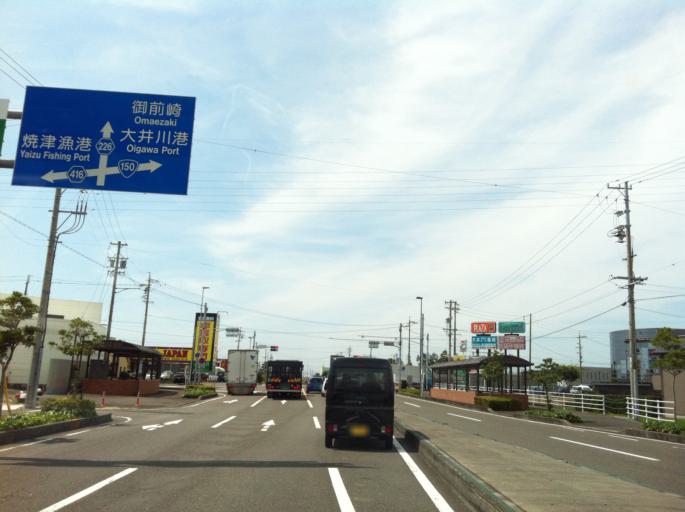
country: JP
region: Shizuoka
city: Yaizu
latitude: 34.8308
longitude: 138.3009
